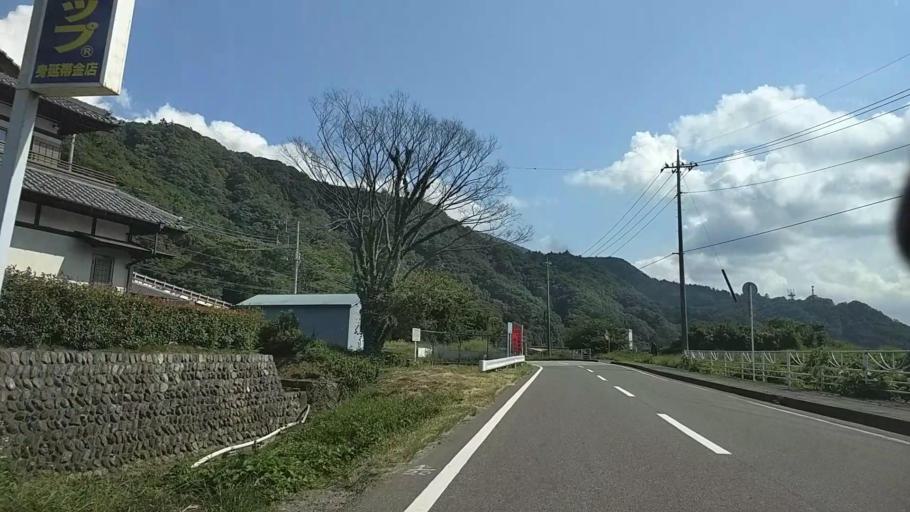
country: JP
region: Shizuoka
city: Fujinomiya
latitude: 35.3859
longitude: 138.4535
